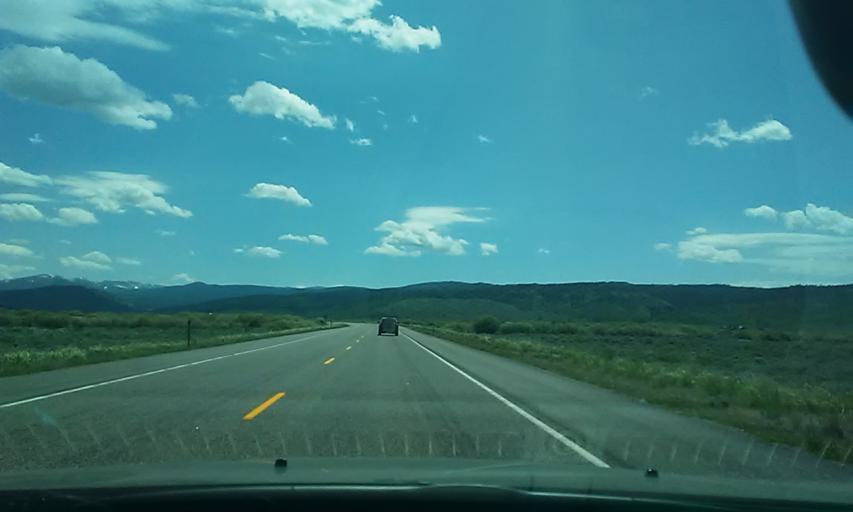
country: US
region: Wyoming
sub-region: Teton County
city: Jackson
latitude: 43.8340
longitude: -110.4274
